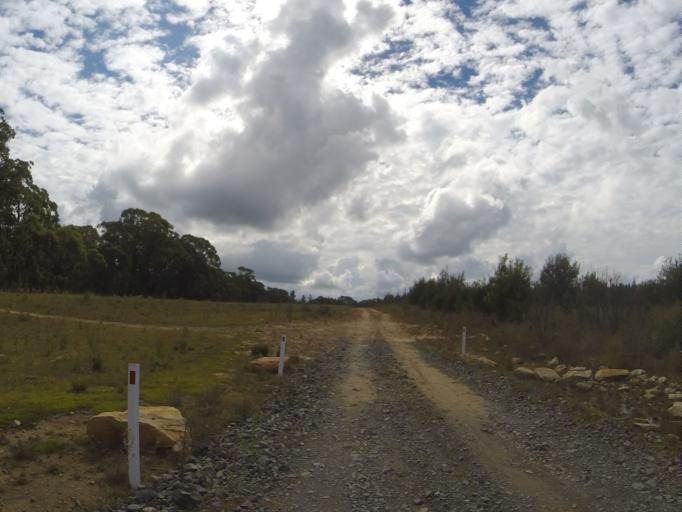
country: AU
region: New South Wales
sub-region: Wingecarribee
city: Moss Vale
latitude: -34.5223
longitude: 150.2250
